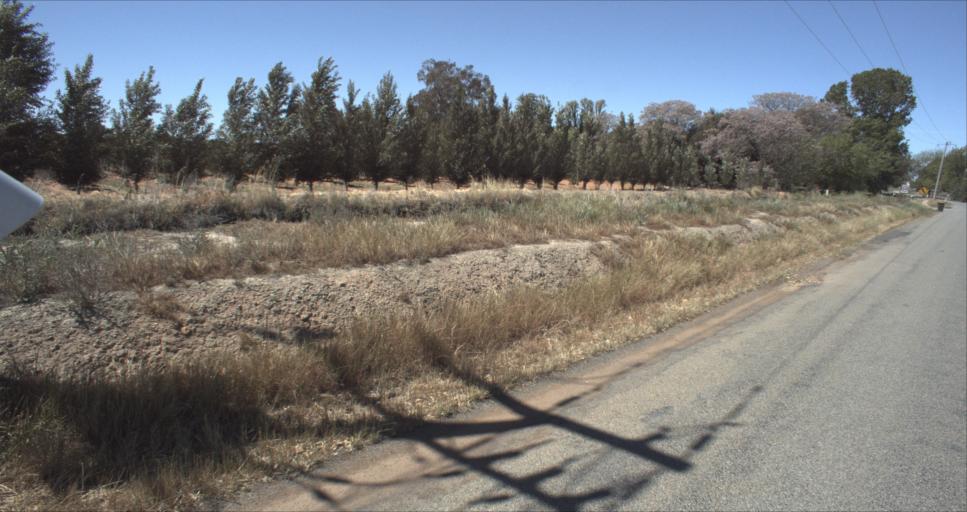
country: AU
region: New South Wales
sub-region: Leeton
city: Leeton
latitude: -34.5479
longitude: 146.3705
